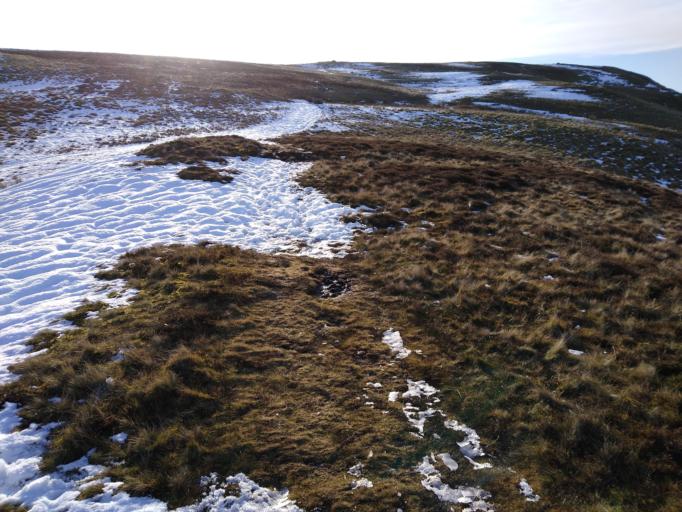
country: GB
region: England
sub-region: Cumbria
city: Penrith
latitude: 54.5841
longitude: -2.8289
